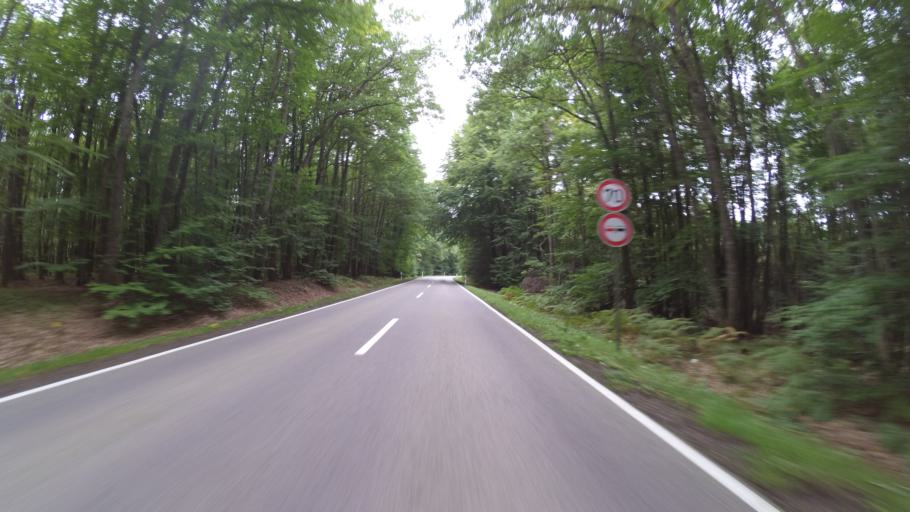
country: DE
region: Saarland
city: Weiskirchen
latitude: 49.5601
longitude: 6.7905
